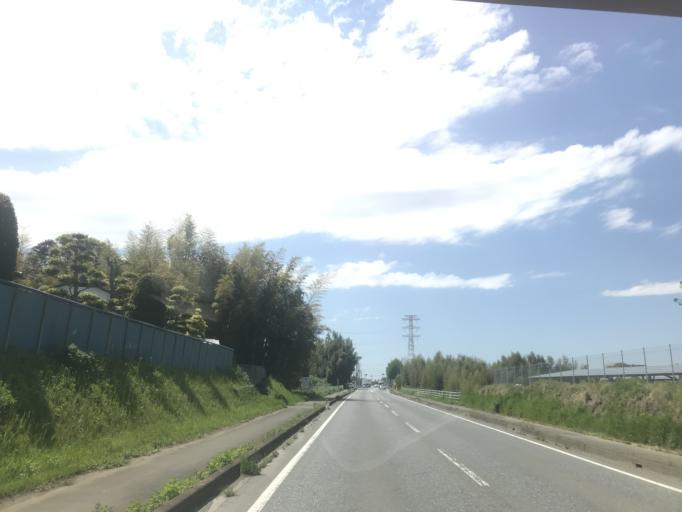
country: JP
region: Chiba
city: Noda
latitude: 35.9668
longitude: 139.8964
